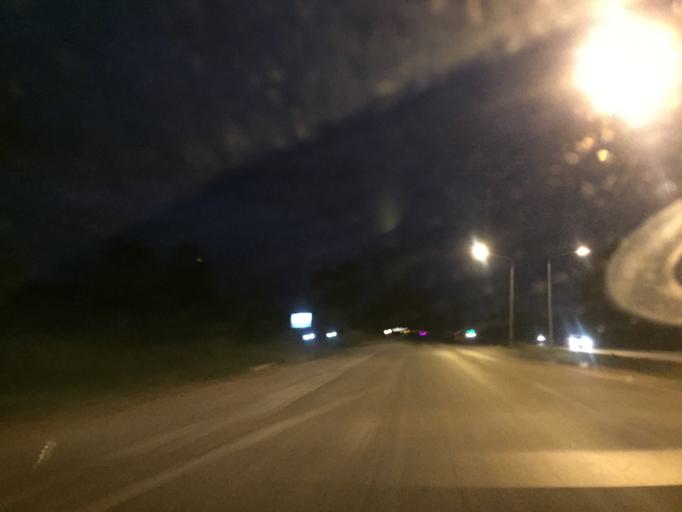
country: TH
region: Changwat Nong Bua Lamphu
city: Na Klang
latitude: 17.2934
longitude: 102.2553
